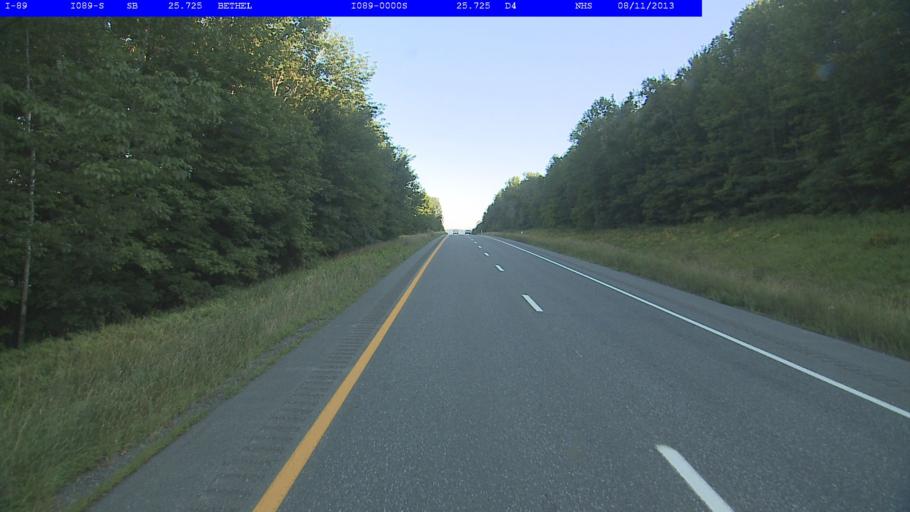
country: US
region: Vermont
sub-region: Orange County
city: Randolph
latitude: 43.8717
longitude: -72.6124
